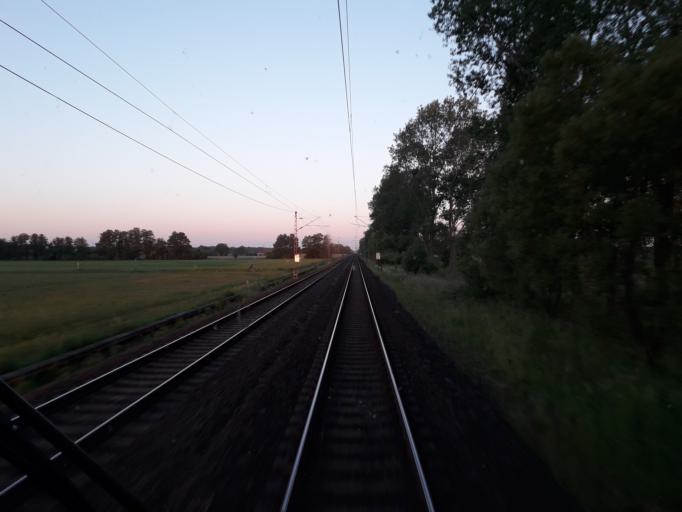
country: DE
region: Brandenburg
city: Hennigsdorf
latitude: 52.6481
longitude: 13.1640
